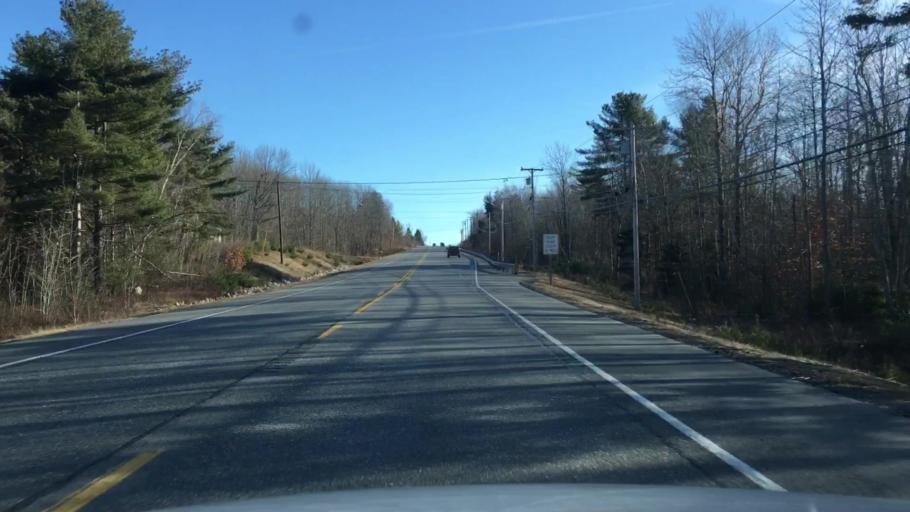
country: US
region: Maine
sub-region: Hancock County
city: Dedham
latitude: 44.6309
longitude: -68.5414
